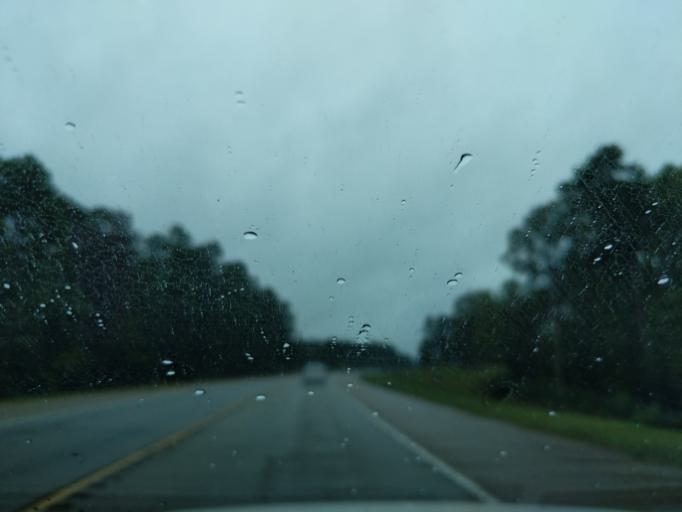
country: US
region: Louisiana
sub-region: Webster Parish
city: Minden
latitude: 32.5932
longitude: -93.2482
